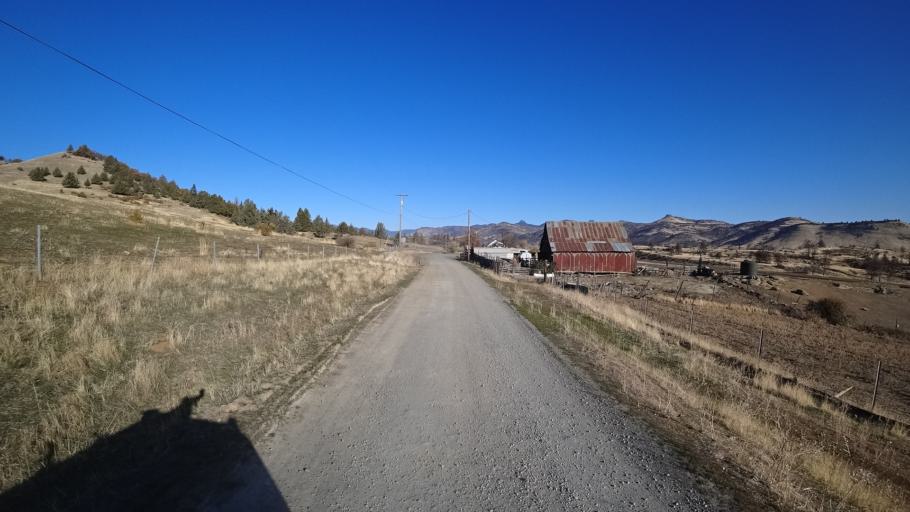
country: US
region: California
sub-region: Siskiyou County
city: Montague
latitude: 41.8923
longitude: -122.5641
